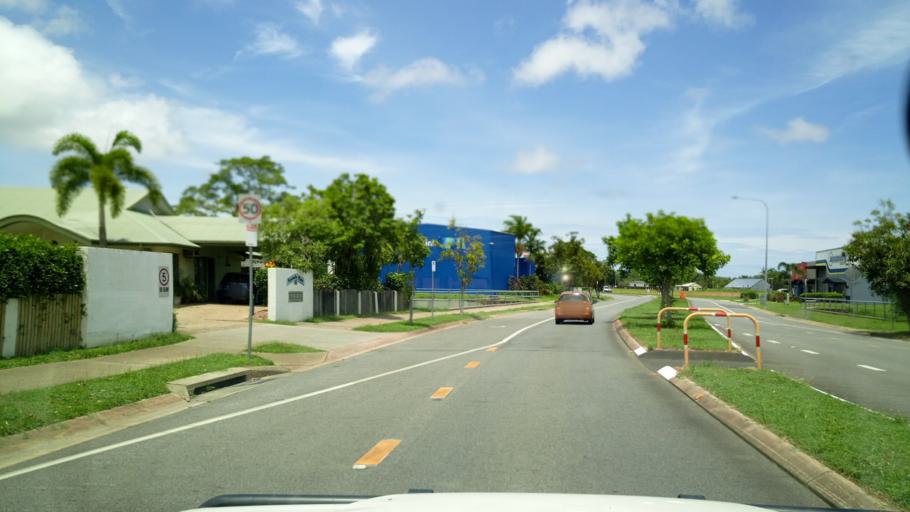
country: AU
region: Queensland
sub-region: Cairns
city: Yorkeys Knob
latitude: -16.8373
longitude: 145.6951
